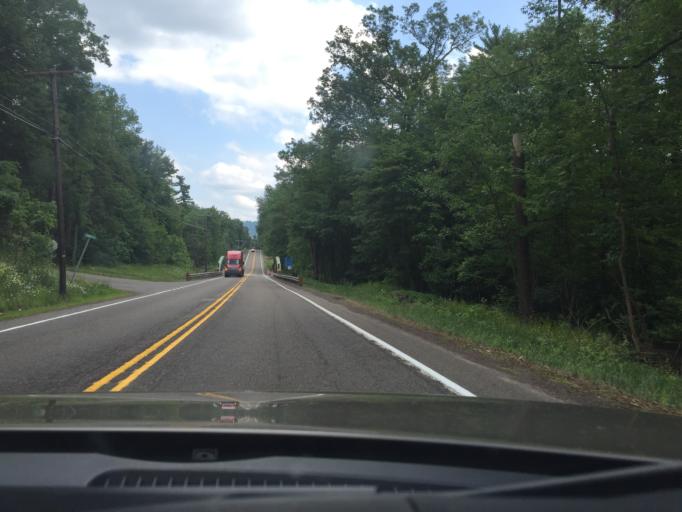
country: US
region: Pennsylvania
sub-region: Luzerne County
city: Conyngham
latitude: 41.0155
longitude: -76.0793
